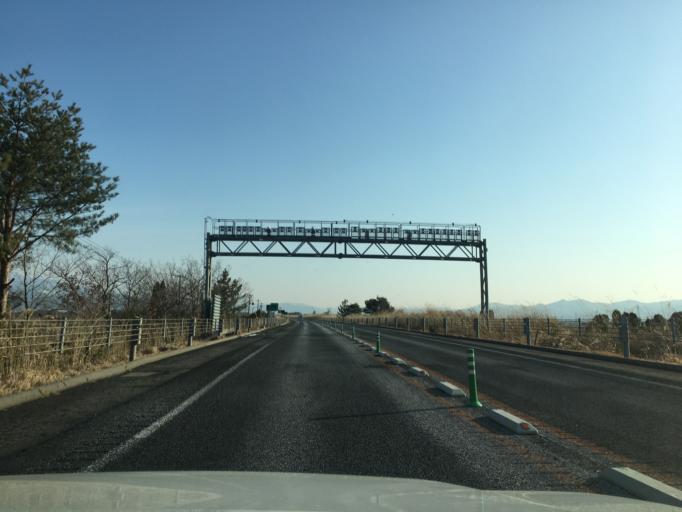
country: JP
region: Yamagata
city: Sagae
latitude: 38.3307
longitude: 140.2974
